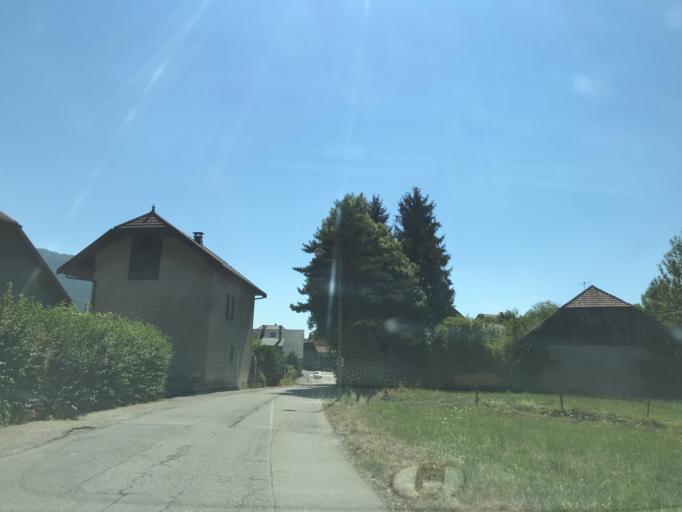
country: FR
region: Rhone-Alpes
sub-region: Departement de la Haute-Savoie
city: Villaz
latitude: 45.9360
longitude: 6.1921
